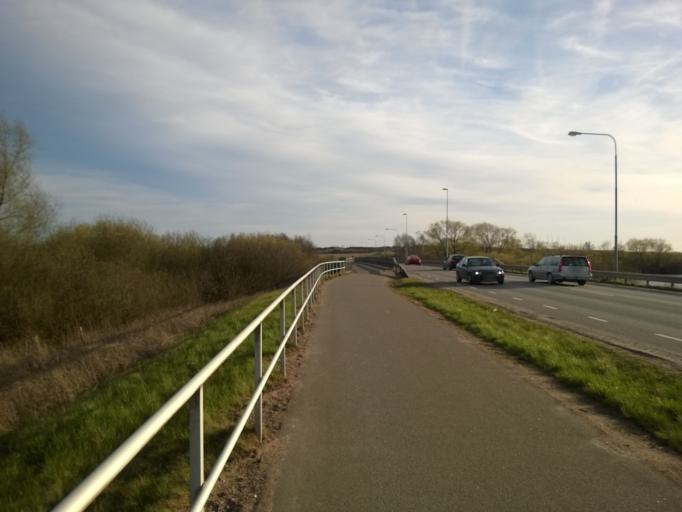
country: SE
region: Skane
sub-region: Kristianstads Kommun
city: Kristianstad
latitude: 56.0332
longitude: 14.1403
